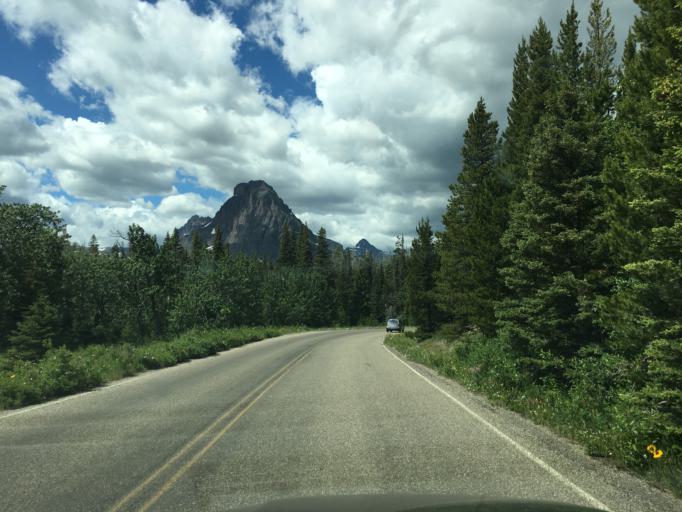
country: US
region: Montana
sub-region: Glacier County
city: South Browning
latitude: 48.4853
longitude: -113.3620
